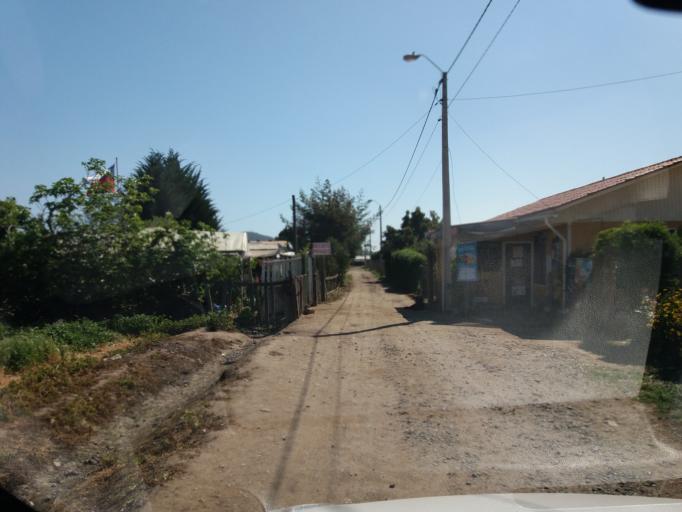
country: CL
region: Valparaiso
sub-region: Provincia de Quillota
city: Quillota
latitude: -32.9405
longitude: -71.2879
